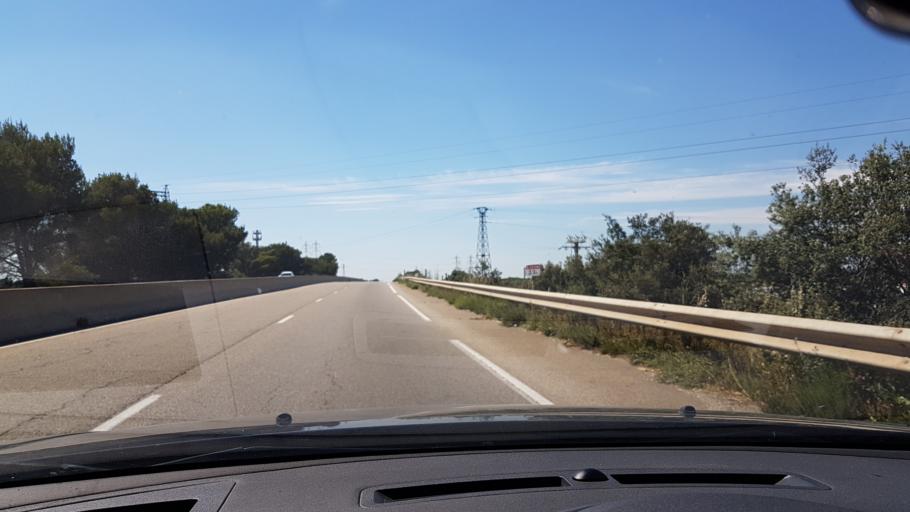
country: FR
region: Provence-Alpes-Cote d'Azur
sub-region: Departement des Bouches-du-Rhone
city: Fos-sur-Mer
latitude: 43.4731
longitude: 4.9046
